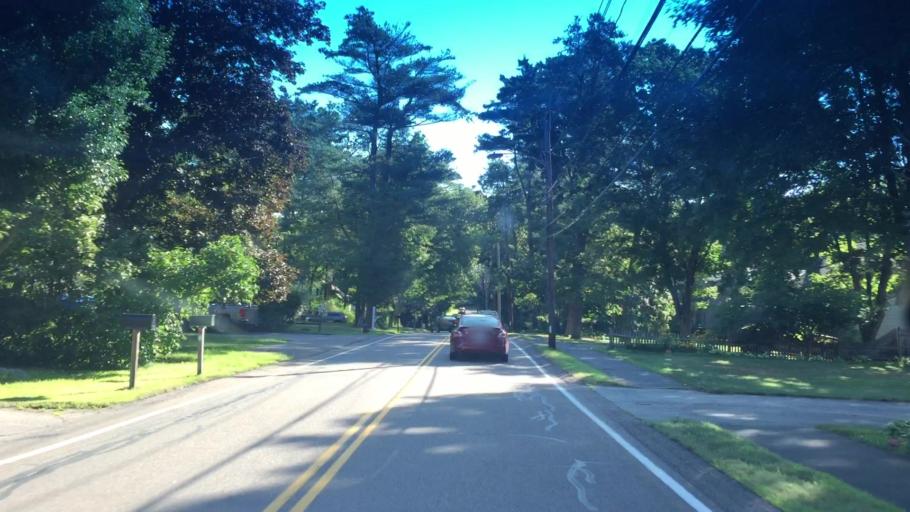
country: US
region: Massachusetts
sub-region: Norfolk County
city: Walpole
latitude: 42.1379
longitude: -71.2813
